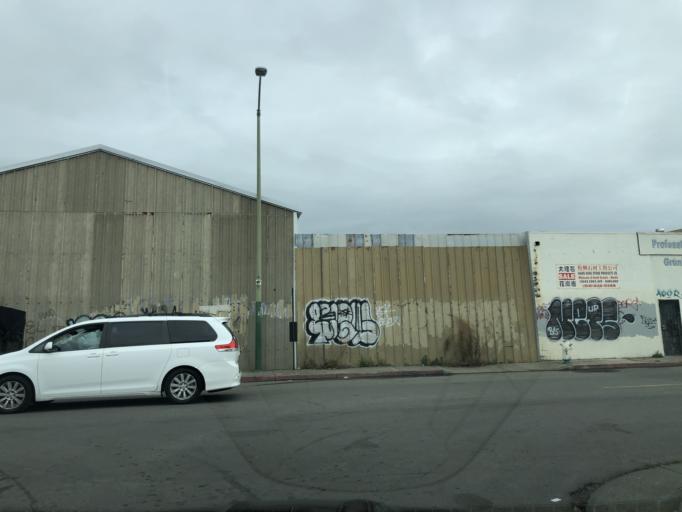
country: US
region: California
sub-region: Alameda County
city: San Leandro
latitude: 37.7347
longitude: -122.1802
